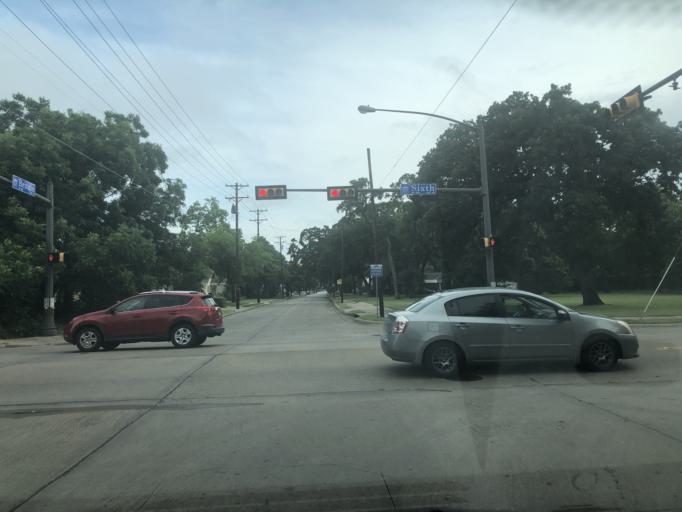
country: US
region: Texas
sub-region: Dallas County
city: Irving
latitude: 32.8084
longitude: -96.9424
